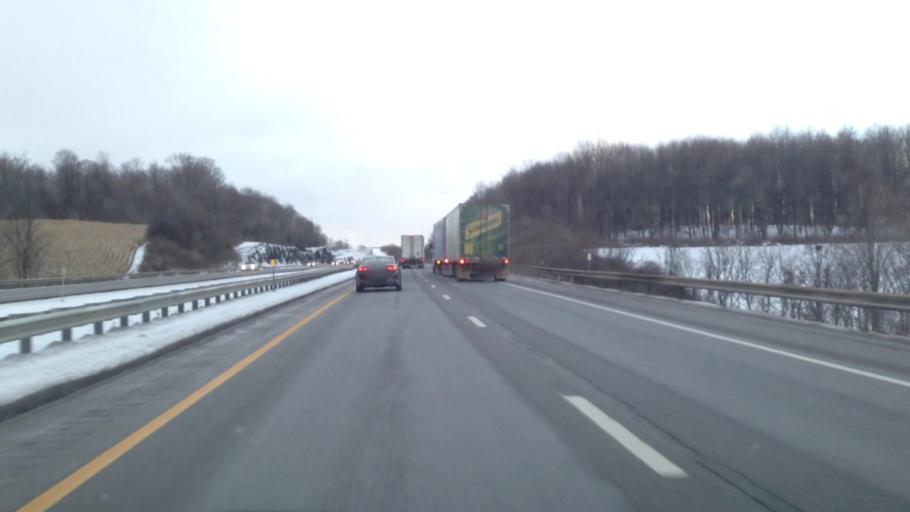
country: US
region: New York
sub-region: Herkimer County
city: Little Falls
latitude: 43.0105
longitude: -74.8435
